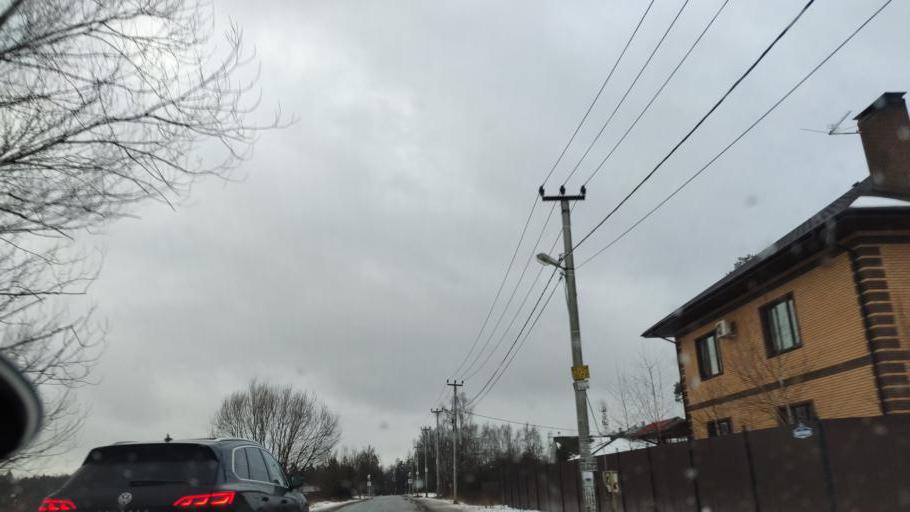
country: RU
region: Moskovskaya
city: Vatutinki
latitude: 55.4580
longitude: 37.3997
